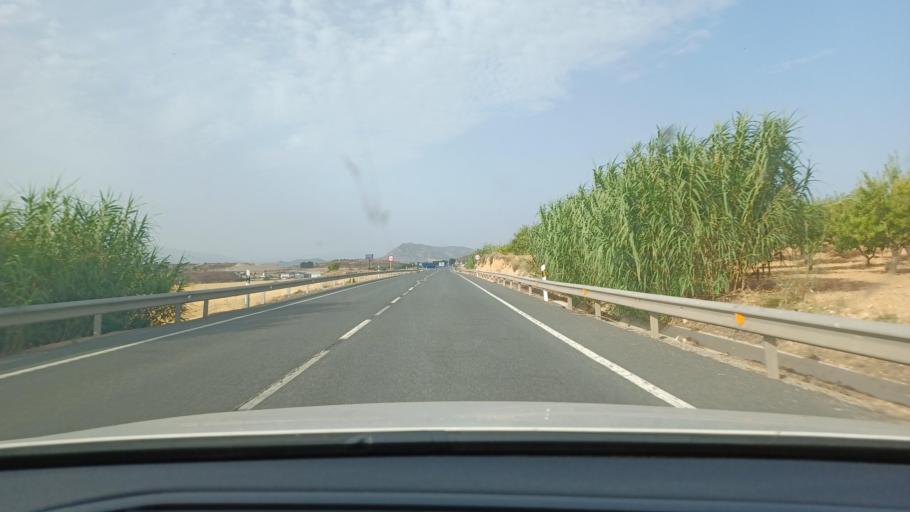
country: ES
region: Castille-La Mancha
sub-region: Provincia de Albacete
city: Caudete
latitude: 38.7363
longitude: -0.9339
